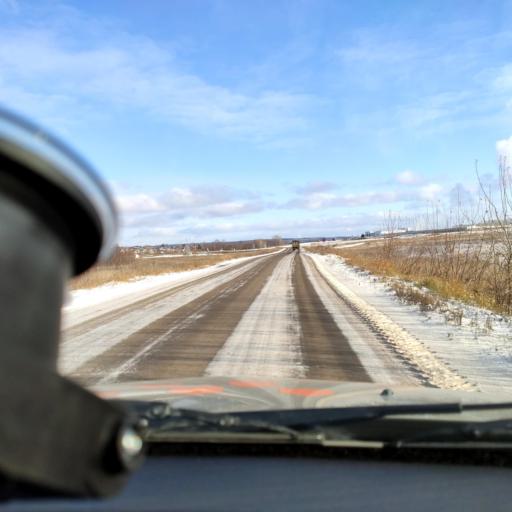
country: RU
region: Bashkortostan
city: Mikhaylovka
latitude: 54.7947
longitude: 55.7712
